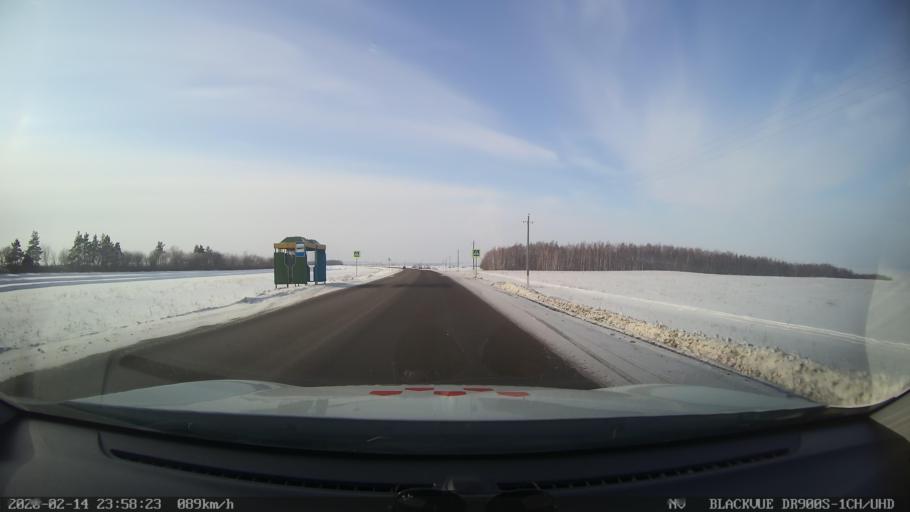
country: RU
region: Tatarstan
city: Kuybyshevskiy Zaton
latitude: 55.3405
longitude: 49.0884
